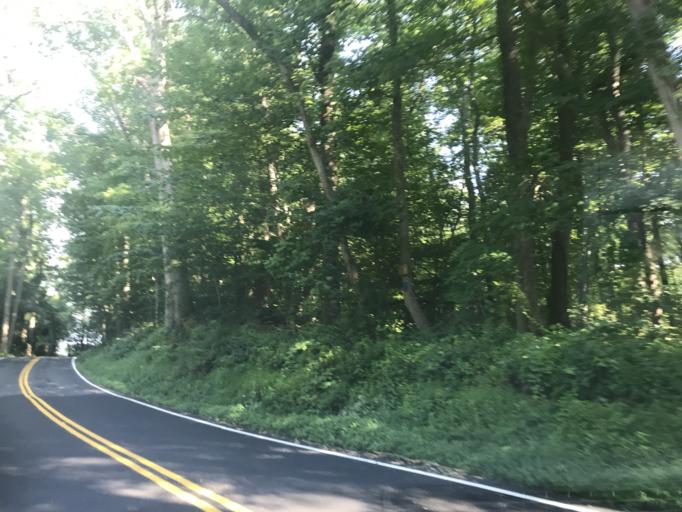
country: US
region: Maryland
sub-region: Harford County
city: Aberdeen
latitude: 39.5188
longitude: -76.1255
